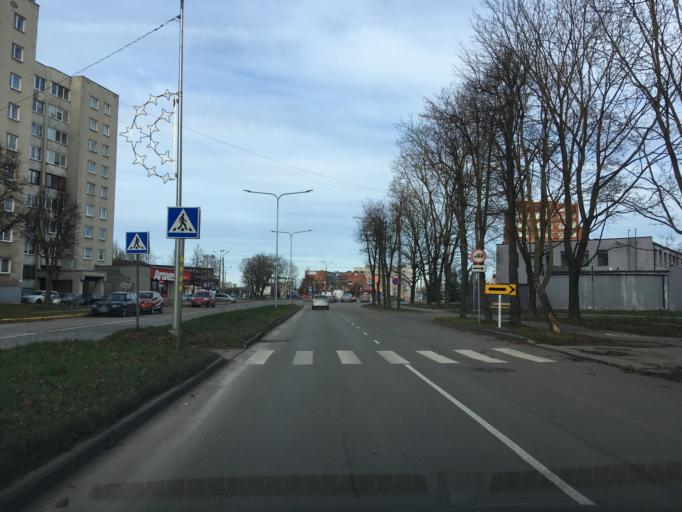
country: EE
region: Ida-Virumaa
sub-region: Narva linn
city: Narva
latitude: 59.3782
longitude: 28.1800
